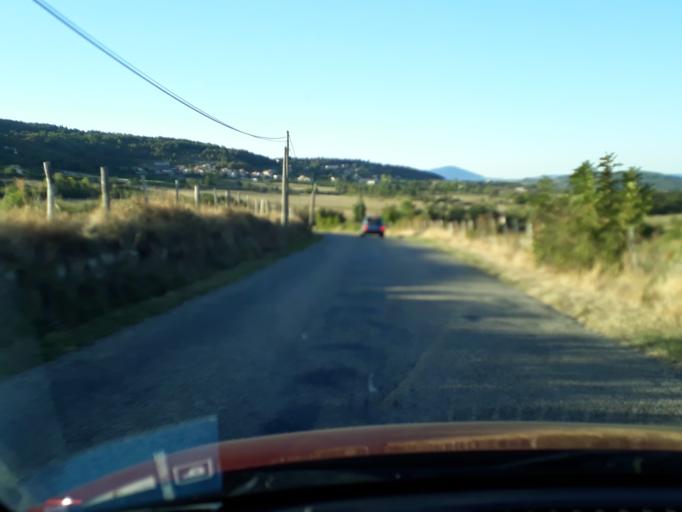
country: FR
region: Rhone-Alpes
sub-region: Departement de l'Ardeche
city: Felines
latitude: 45.3234
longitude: 4.7127
